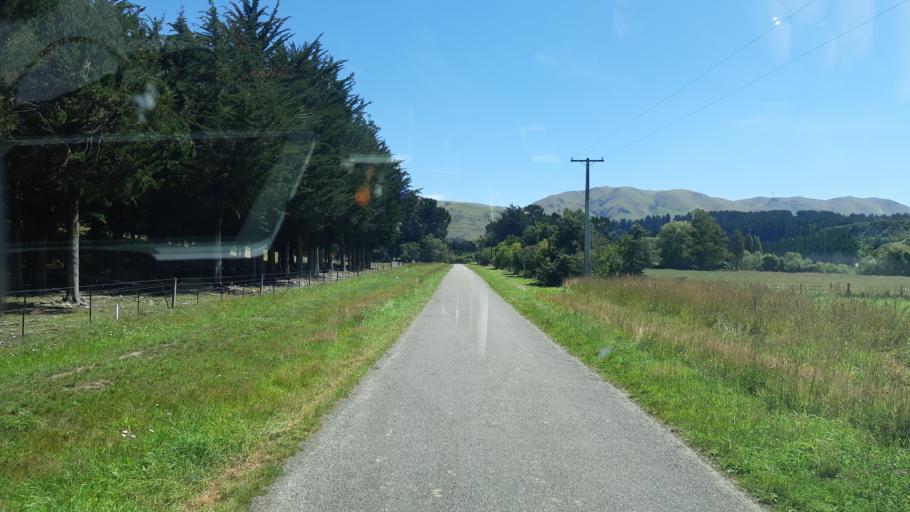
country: NZ
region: Canterbury
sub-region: Timaru District
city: Pleasant Point
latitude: -44.3327
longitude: 170.8789
